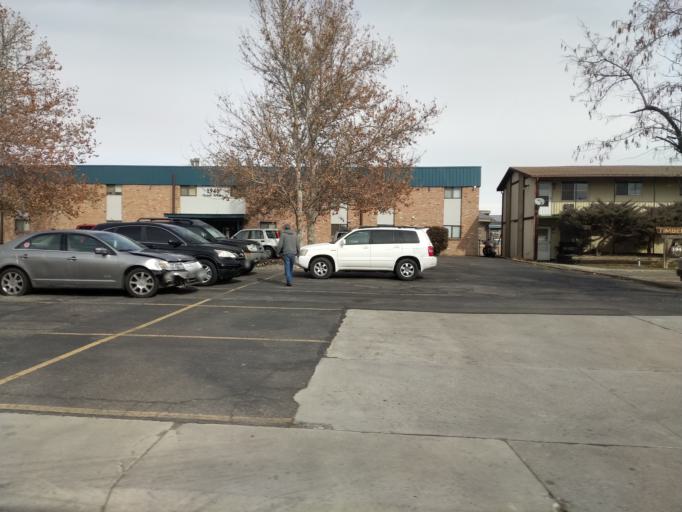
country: US
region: Colorado
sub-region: Mesa County
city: Grand Junction
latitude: 39.0701
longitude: -108.5411
